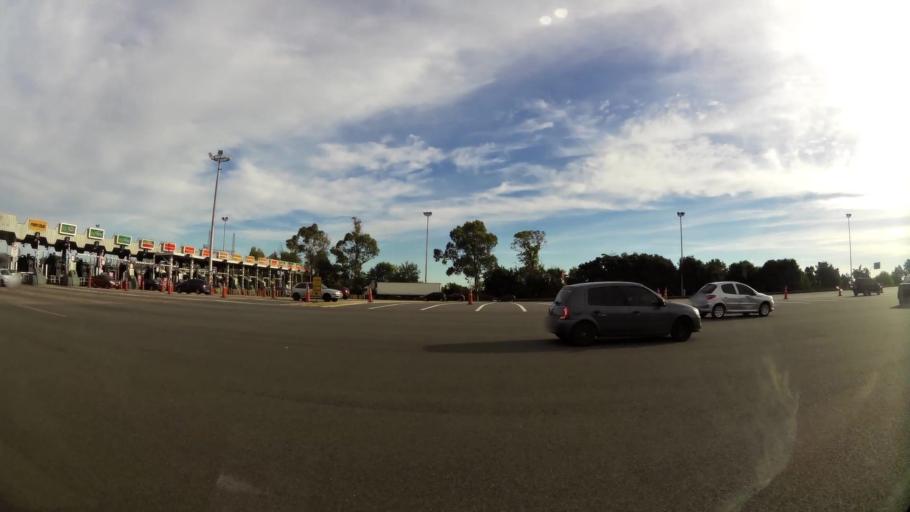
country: AR
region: Buenos Aires F.D.
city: Villa Lugano
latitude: -34.6475
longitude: -58.4785
